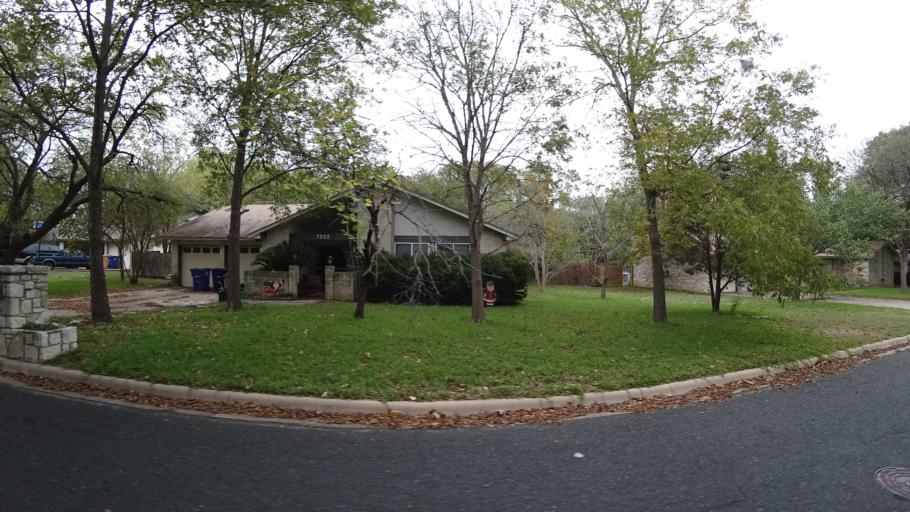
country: US
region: Texas
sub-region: Travis County
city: Barton Creek
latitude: 30.2359
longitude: -97.8866
